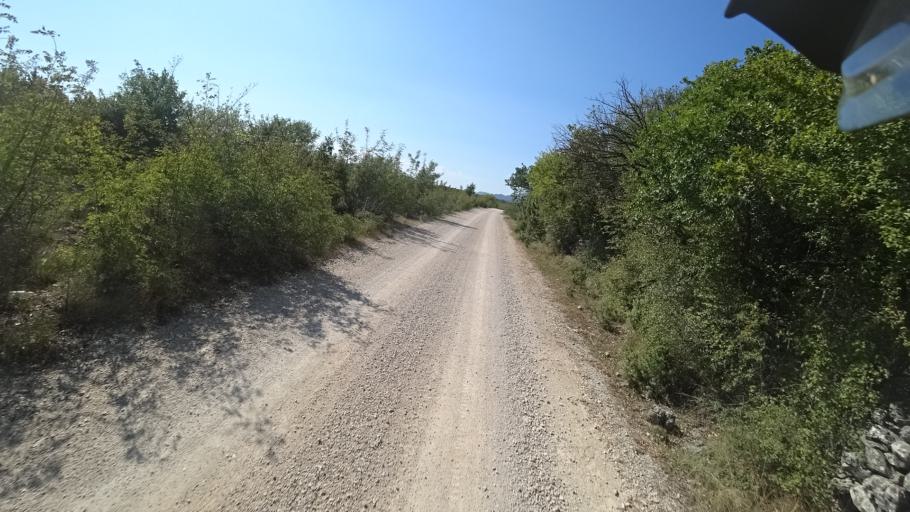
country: HR
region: Sibensko-Kniniska
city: Knin
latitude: 43.9960
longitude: 16.1933
